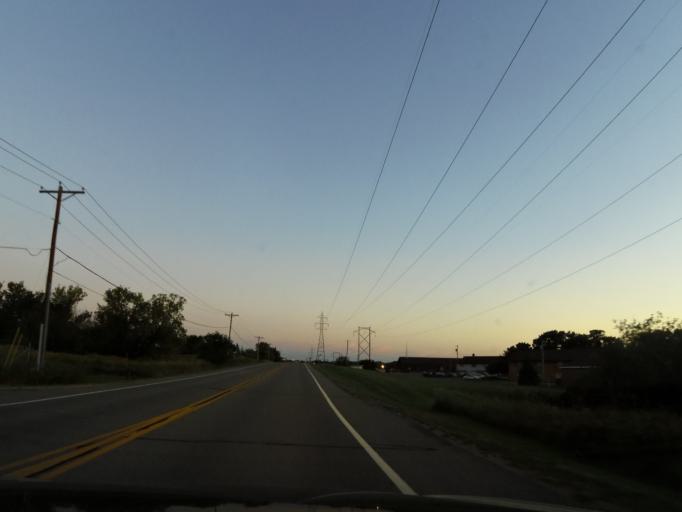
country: US
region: Minnesota
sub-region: Washington County
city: Oakdale
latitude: 44.9525
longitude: -92.9646
